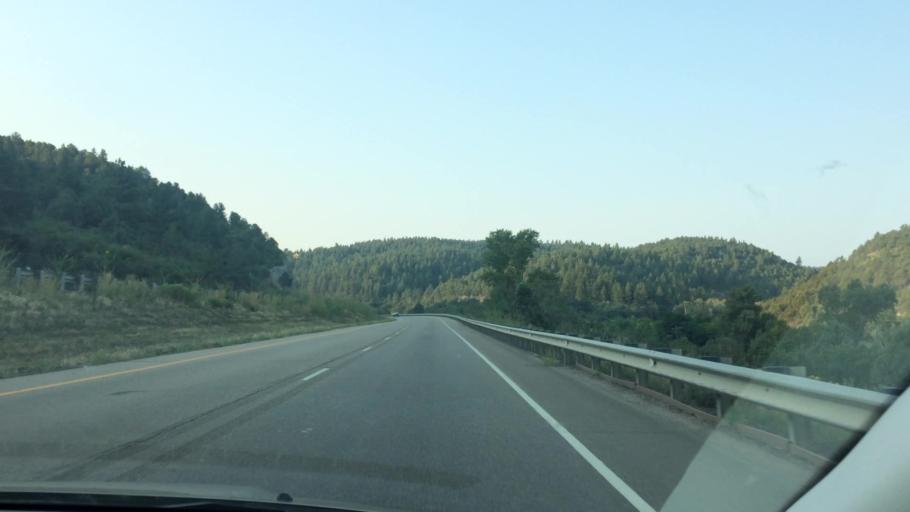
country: US
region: Colorado
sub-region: Las Animas County
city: Trinidad
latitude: 37.0548
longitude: -104.5230
